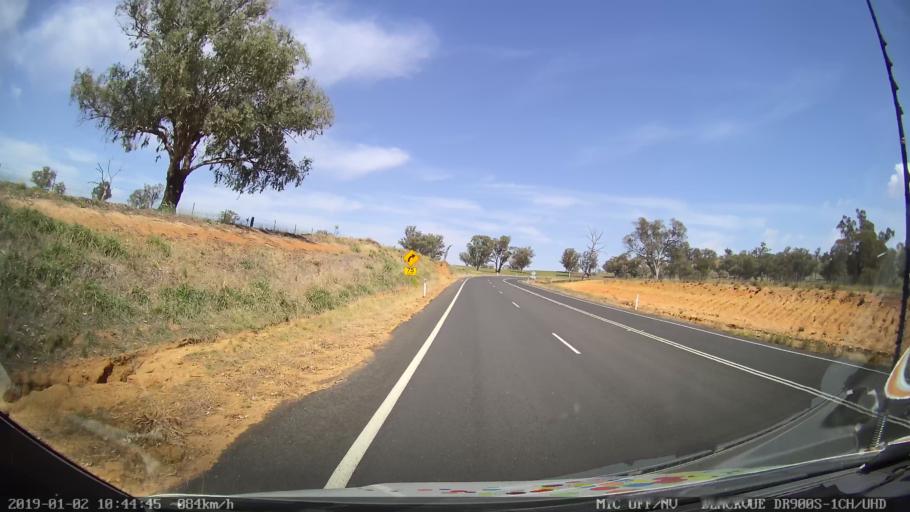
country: AU
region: New South Wales
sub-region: Cootamundra
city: Cootamundra
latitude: -34.7589
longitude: 148.2920
